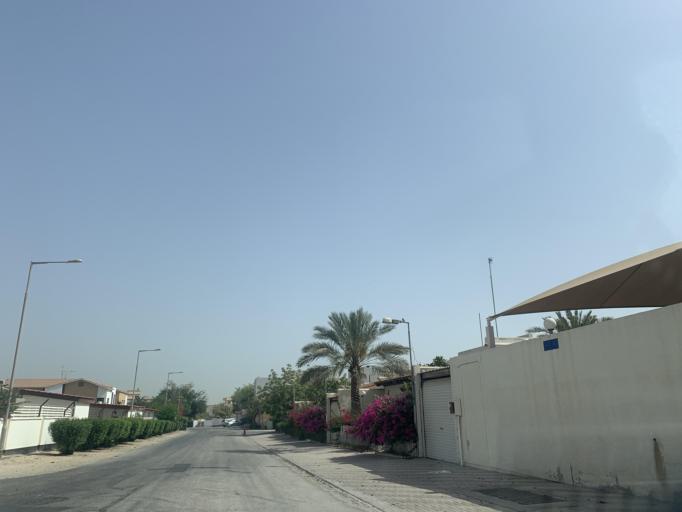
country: BH
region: Northern
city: Madinat `Isa
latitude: 26.1513
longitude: 50.5308
